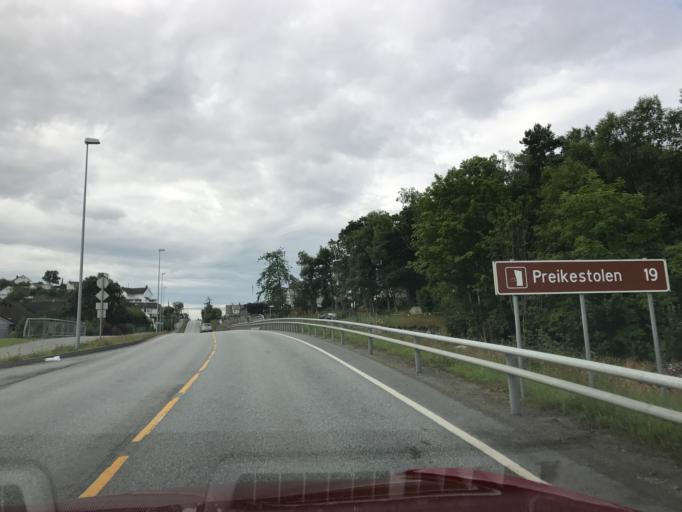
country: NO
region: Rogaland
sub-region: Strand
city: Tau
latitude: 59.0596
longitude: 5.9213
